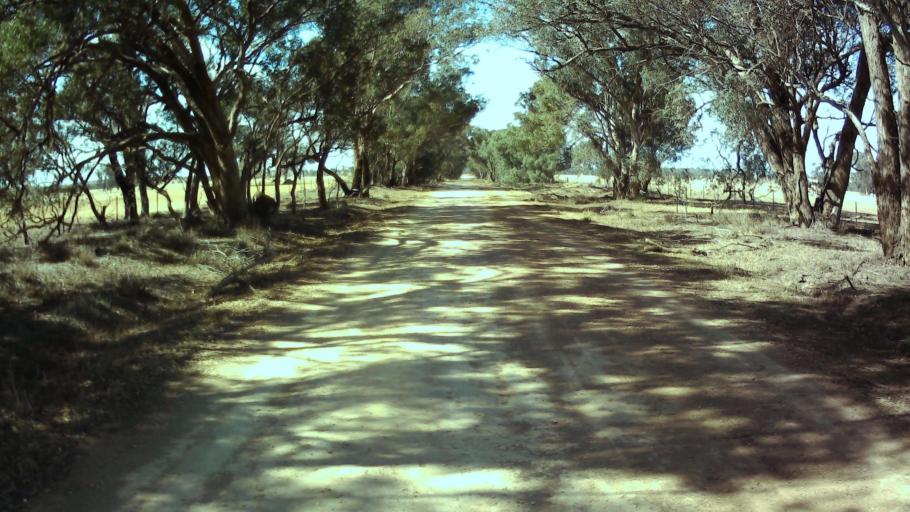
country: AU
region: New South Wales
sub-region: Weddin
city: Grenfell
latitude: -34.0494
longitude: 148.3142
